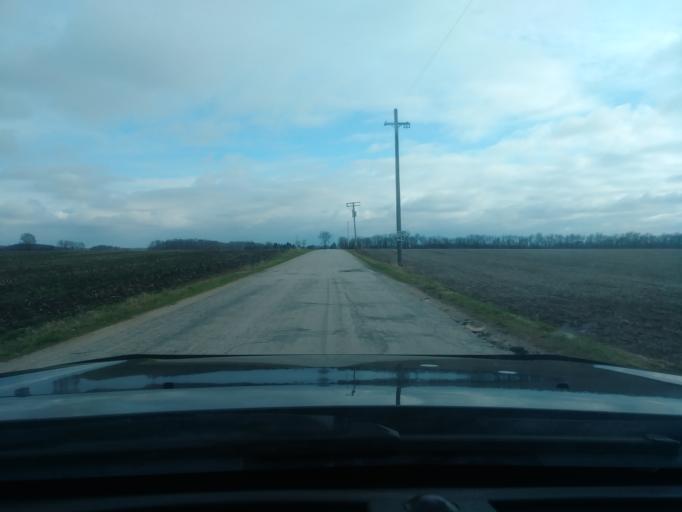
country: US
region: Indiana
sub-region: LaPorte County
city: LaPorte
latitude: 41.5666
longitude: -86.7983
